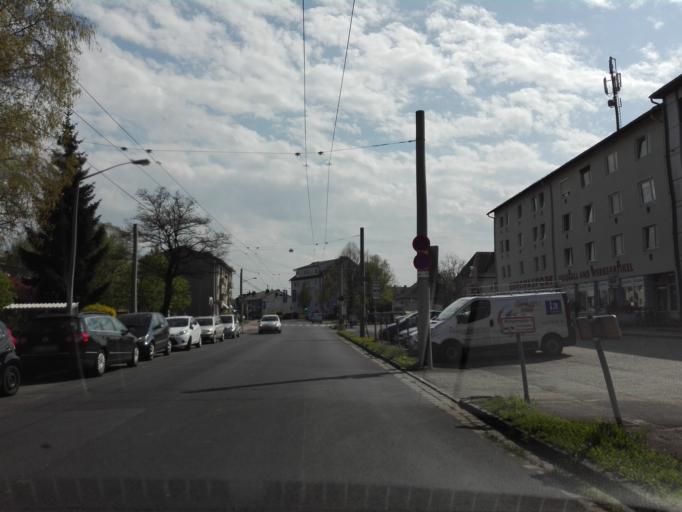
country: AT
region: Upper Austria
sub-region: Politischer Bezirk Linz-Land
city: Ansfelden
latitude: 48.2494
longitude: 14.2847
